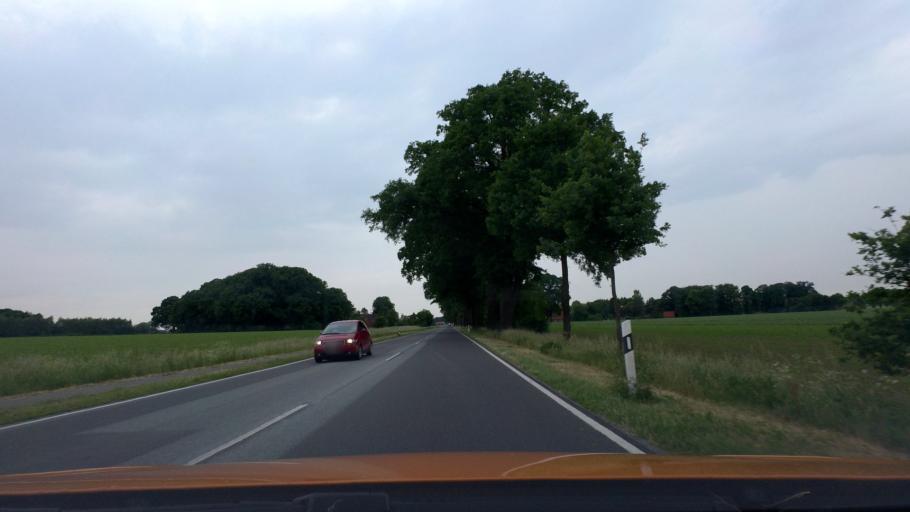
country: DE
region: Lower Saxony
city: Wietzen
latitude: 52.7310
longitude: 9.0378
